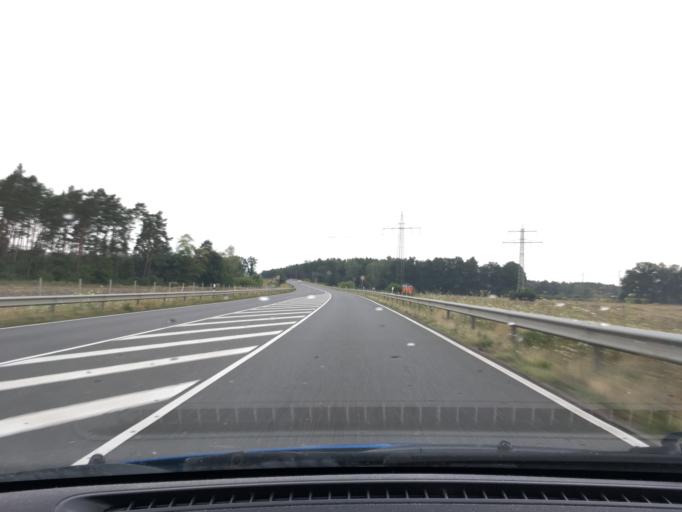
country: DE
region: Lower Saxony
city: Adelheidsdorf
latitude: 52.5724
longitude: 10.0780
